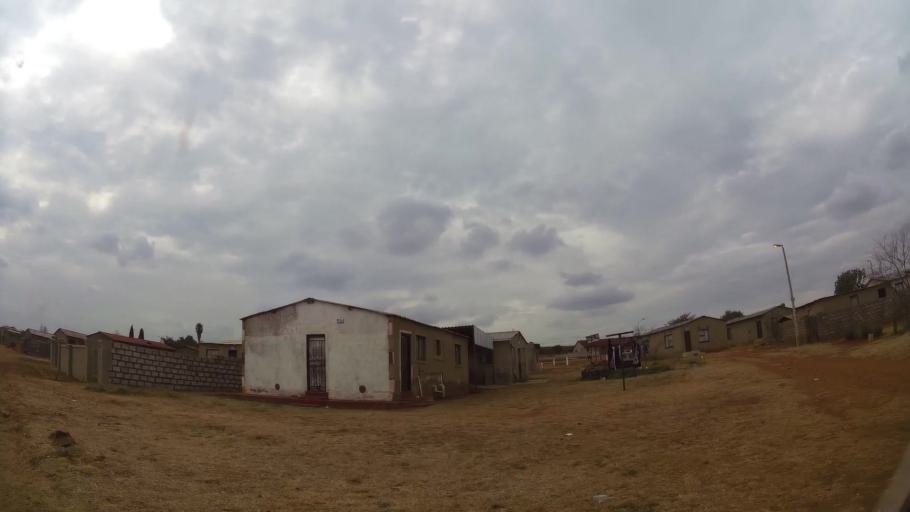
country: ZA
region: Gauteng
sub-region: Ekurhuleni Metropolitan Municipality
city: Germiston
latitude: -26.3805
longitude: 28.1206
